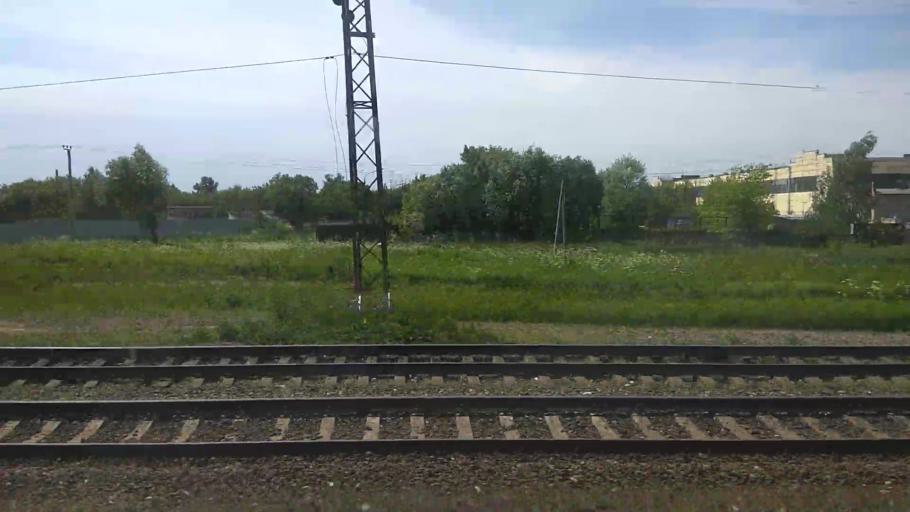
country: RU
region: Moskovskaya
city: Malyshevo
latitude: 55.5022
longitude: 38.3570
